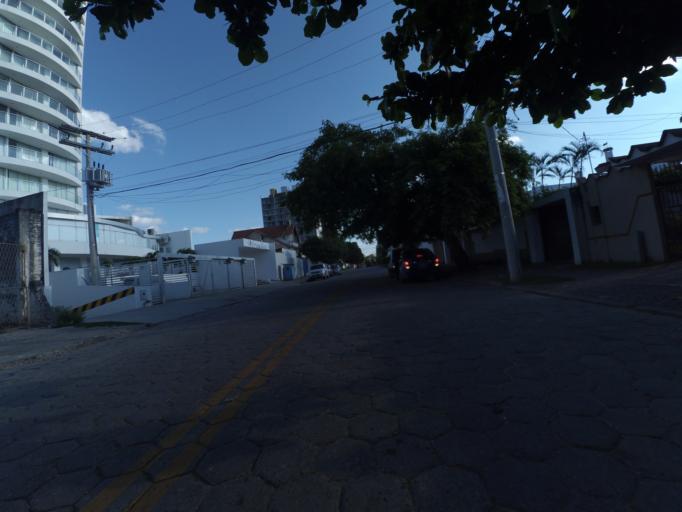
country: BO
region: Santa Cruz
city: Santa Cruz de la Sierra
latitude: -17.7922
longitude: -63.1951
